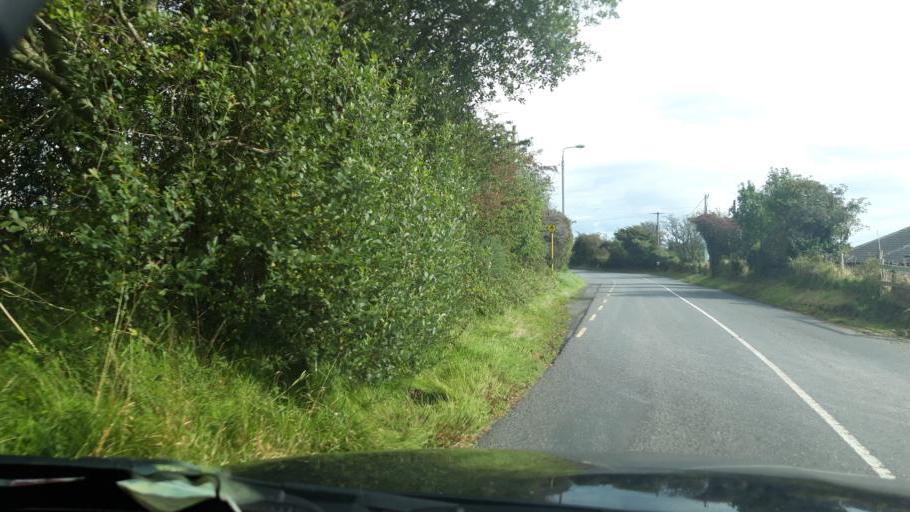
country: IE
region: Leinster
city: Sandyford
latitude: 53.2203
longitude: -6.2296
